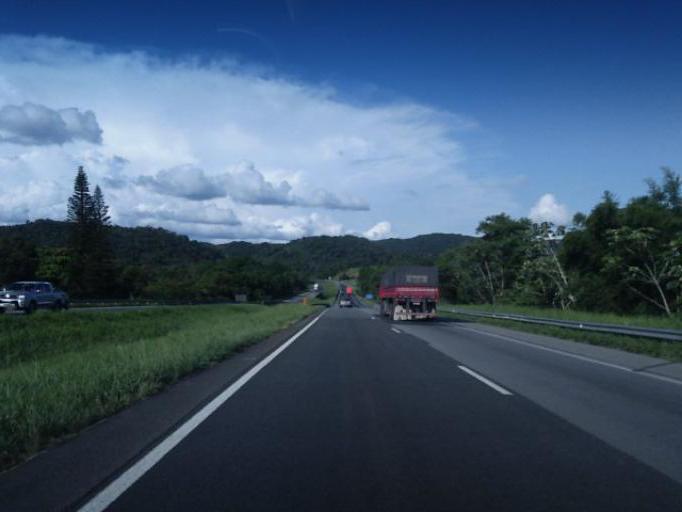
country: BR
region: Sao Paulo
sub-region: Miracatu
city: Miracatu
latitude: -24.2460
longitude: -47.3681
